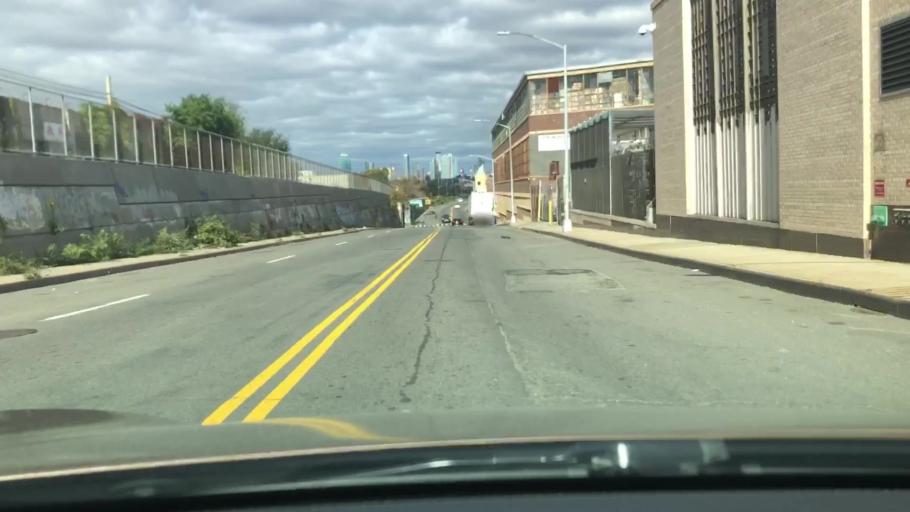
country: US
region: New York
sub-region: Queens County
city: Long Island City
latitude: 40.7185
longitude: -73.9103
